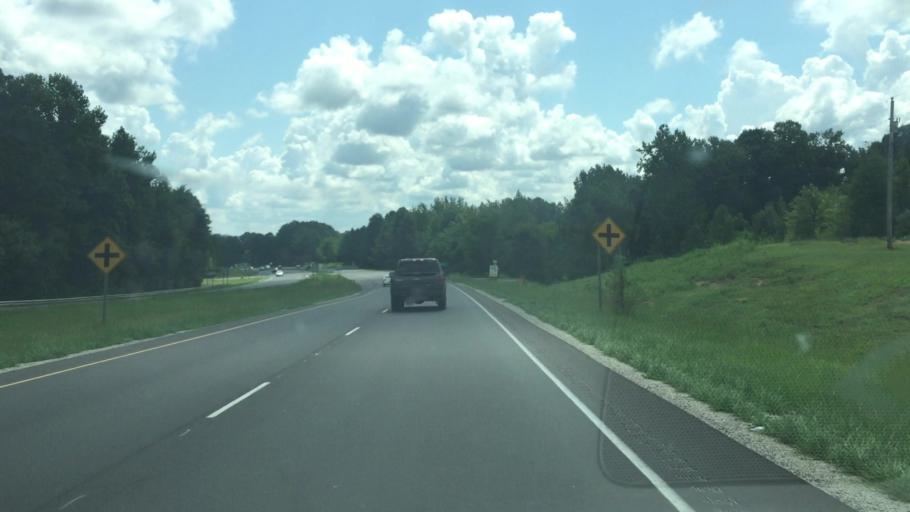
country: US
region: North Carolina
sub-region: Richmond County
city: Cordova
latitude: 34.9448
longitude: -79.8901
